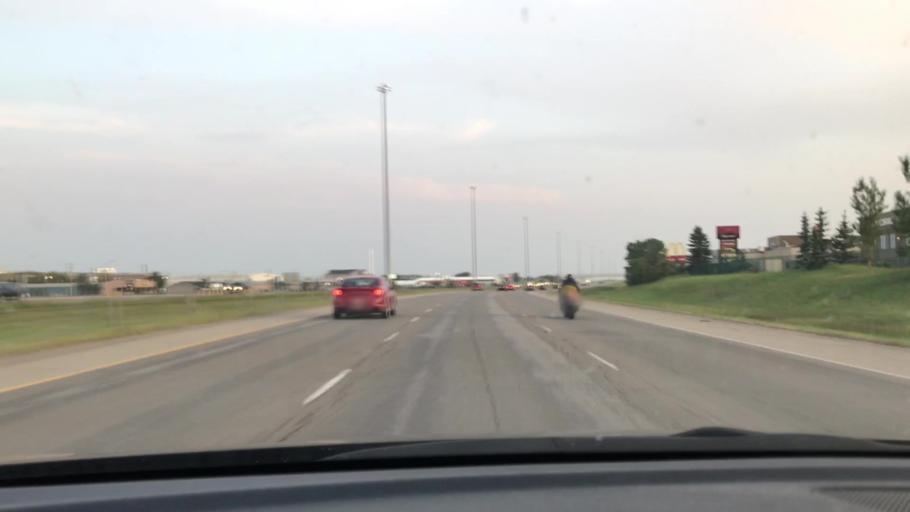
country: CA
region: Alberta
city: Airdrie
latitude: 51.2929
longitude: -114.0002
